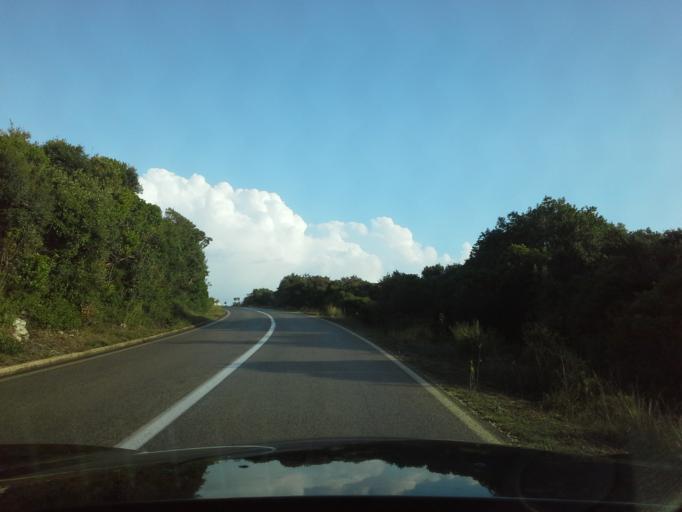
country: HR
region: Primorsko-Goranska
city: Mali Losinj
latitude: 44.5860
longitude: 14.4097
